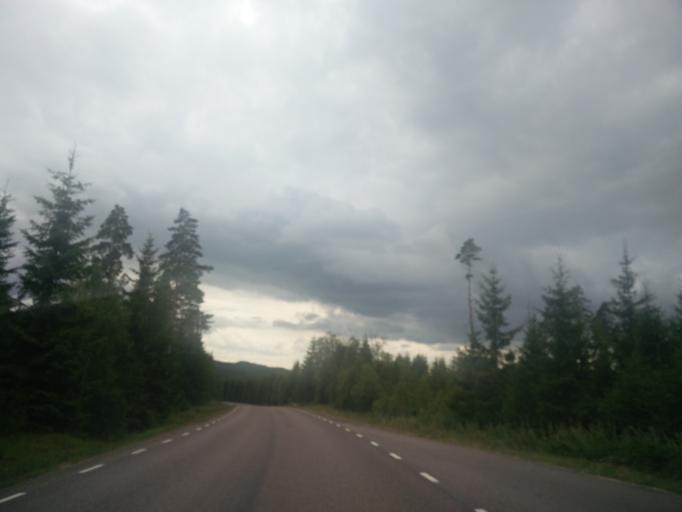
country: SE
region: Vaermland
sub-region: Arvika Kommun
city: Arvika
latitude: 59.9478
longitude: 12.6930
